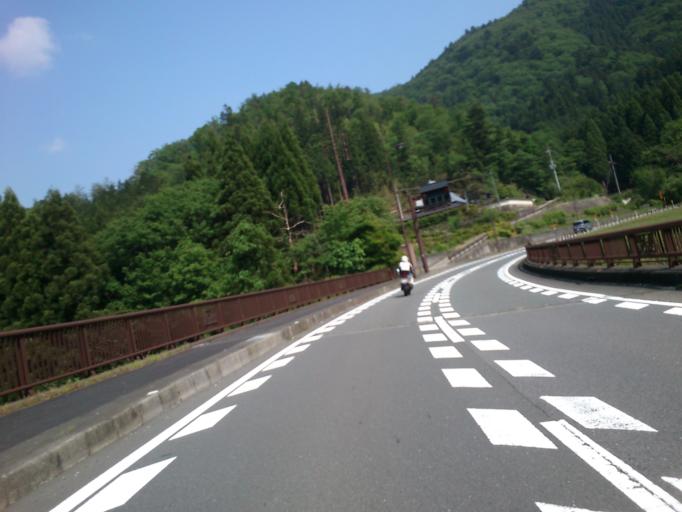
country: JP
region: Kyoto
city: Kameoka
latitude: 35.2313
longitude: 135.5730
